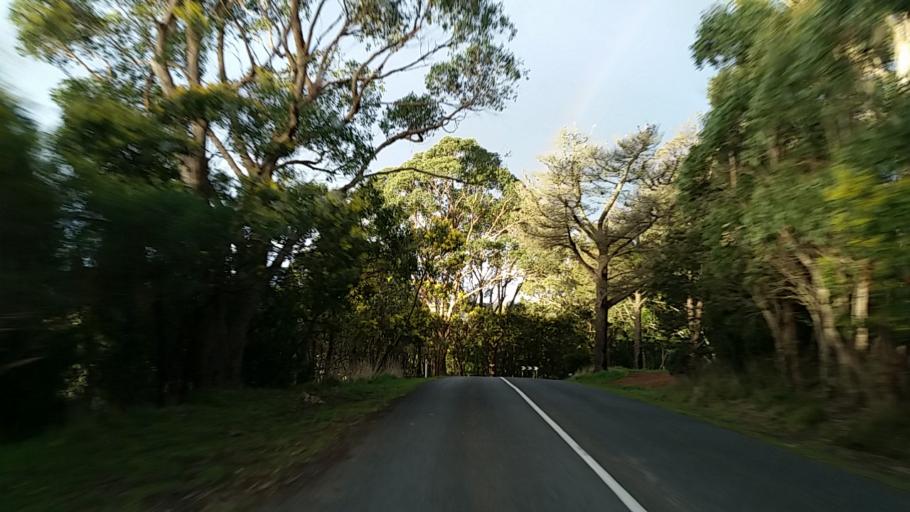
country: AU
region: South Australia
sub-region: Adelaide Hills
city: Lobethal
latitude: -34.8968
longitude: 138.8267
